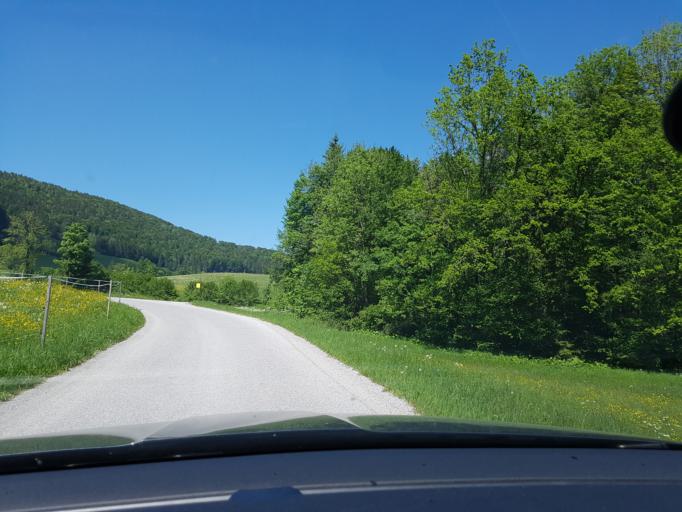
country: AT
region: Salzburg
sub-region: Politischer Bezirk Salzburg-Umgebung
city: Koppl
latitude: 47.7885
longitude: 13.1256
